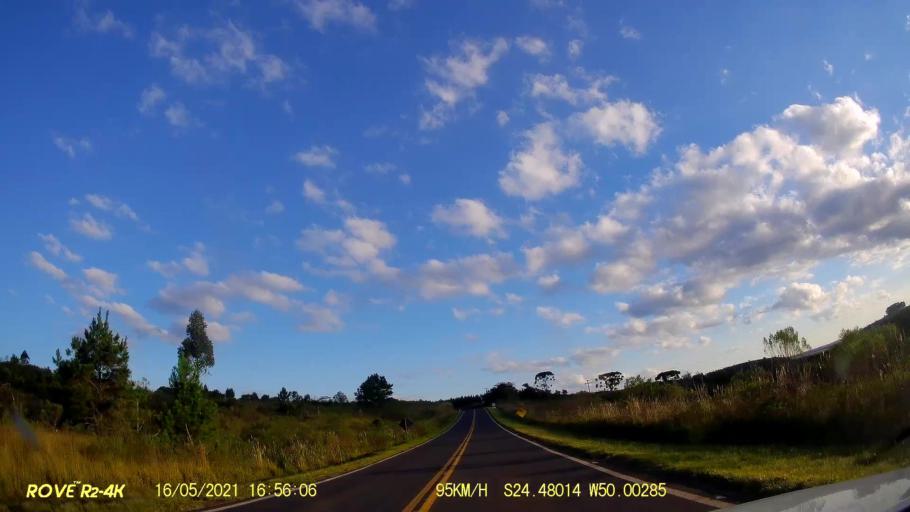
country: BR
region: Parana
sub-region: Pirai Do Sul
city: Pirai do Sul
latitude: -24.4801
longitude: -50.0030
